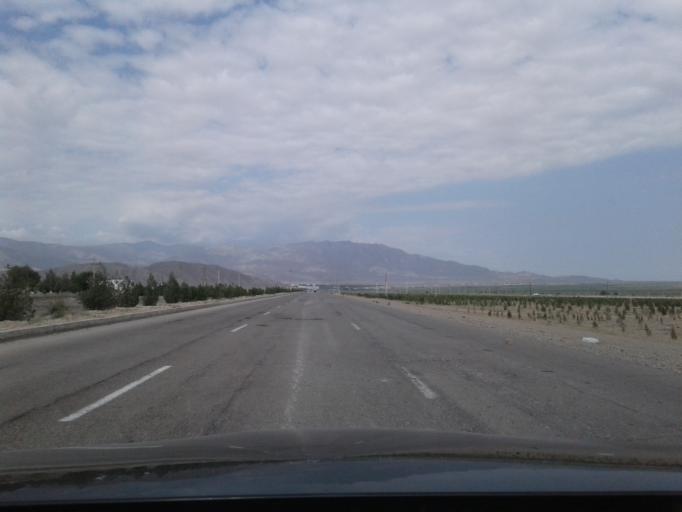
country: TM
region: Ahal
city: Baharly
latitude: 38.5101
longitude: 57.2531
